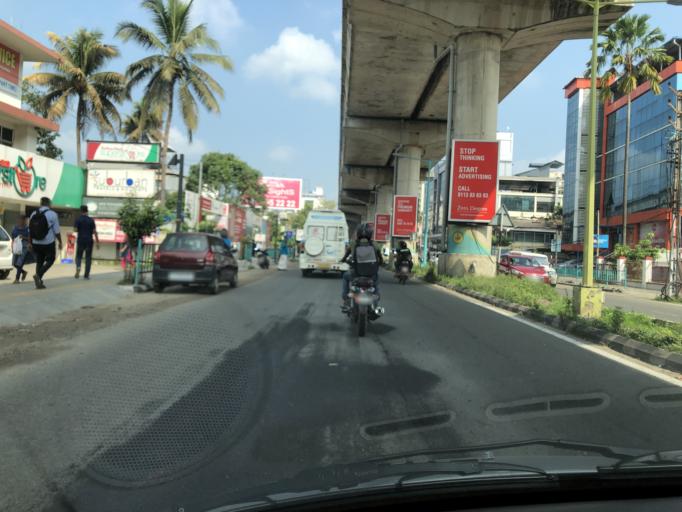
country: IN
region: Kerala
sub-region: Ernakulam
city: Elur
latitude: 10.0082
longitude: 76.3041
